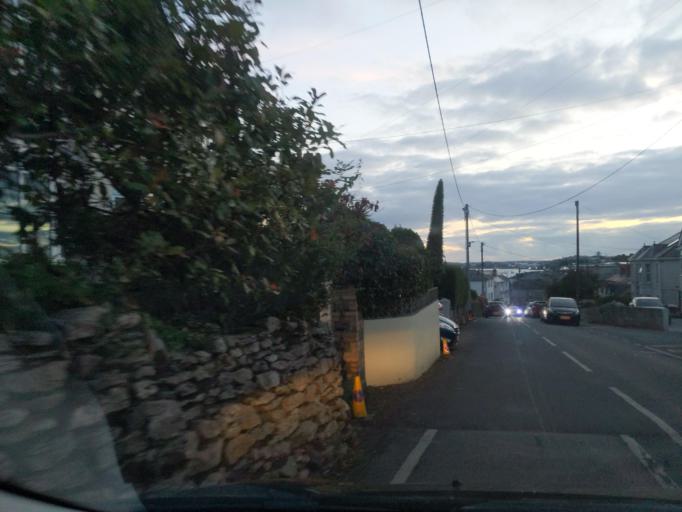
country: GB
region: England
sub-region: Plymouth
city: Plymstock
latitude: 50.3605
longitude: -4.1052
